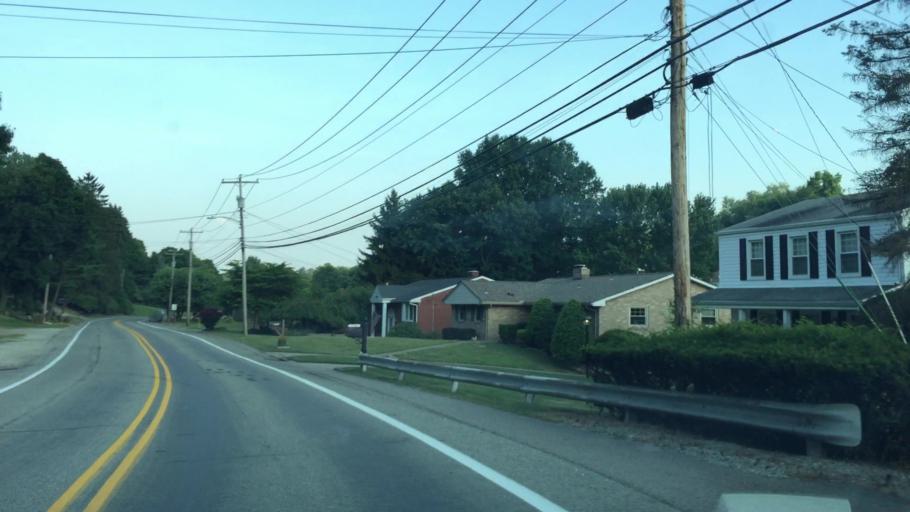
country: US
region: Pennsylvania
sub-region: Allegheny County
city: Bethel Park
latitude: 40.3037
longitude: -80.0565
